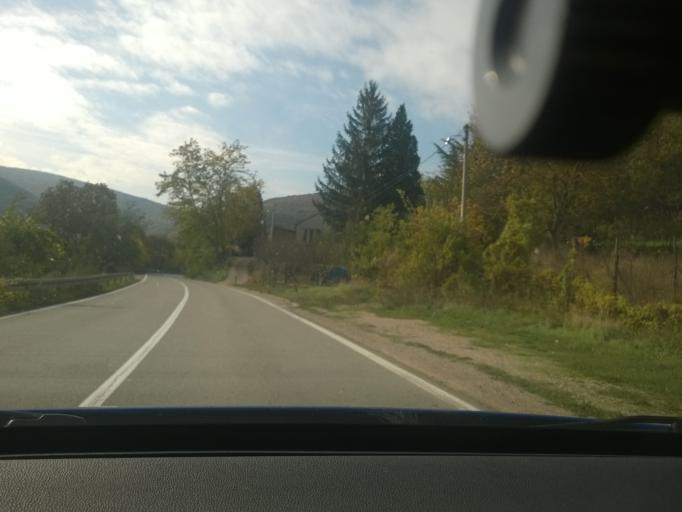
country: RS
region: Central Serbia
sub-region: Nisavski Okrug
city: Svrljig
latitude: 43.3320
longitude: 22.1164
